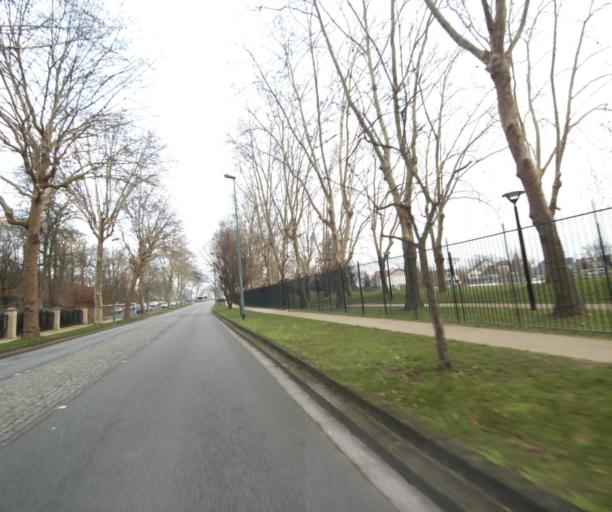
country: FR
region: Ile-de-France
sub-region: Departement des Hauts-de-Seine
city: Suresnes
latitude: 48.8734
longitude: 2.2176
